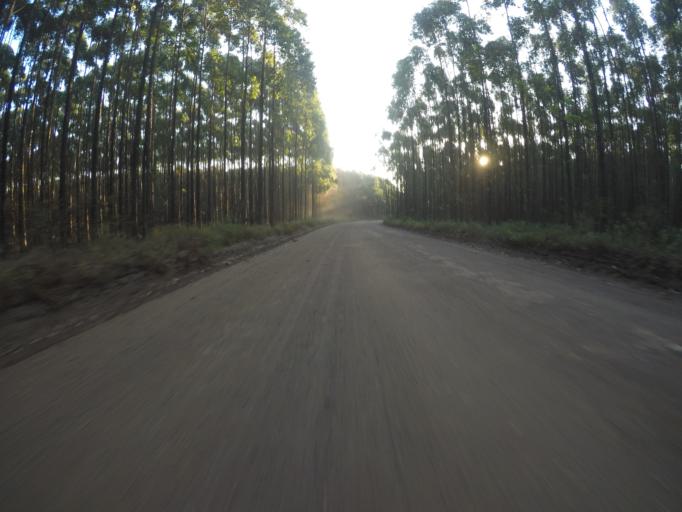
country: ZA
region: KwaZulu-Natal
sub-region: uThungulu District Municipality
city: KwaMbonambi
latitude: -28.6737
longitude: 32.0926
